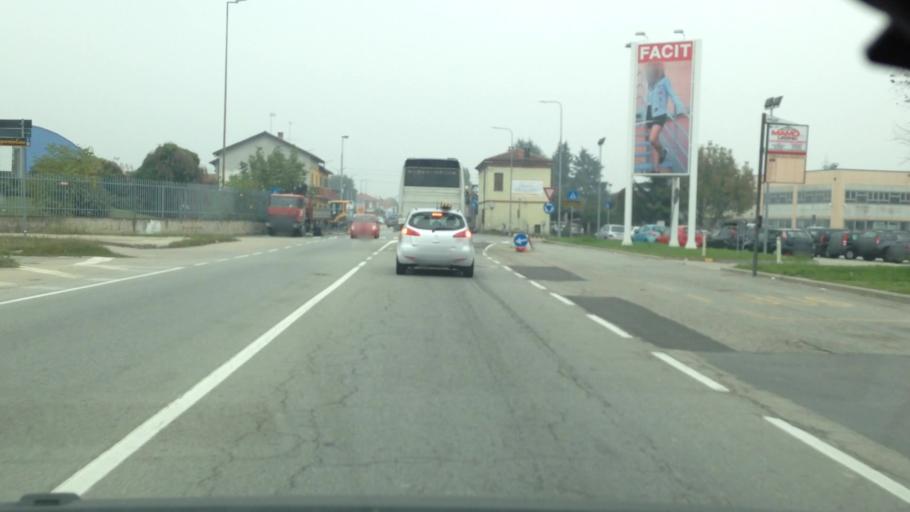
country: IT
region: Piedmont
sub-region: Provincia di Asti
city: Asti
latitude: 44.9059
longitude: 8.2382
